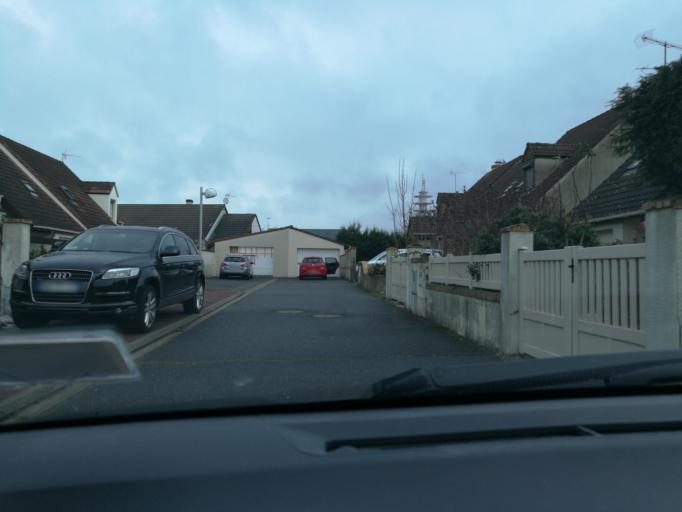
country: FR
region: Centre
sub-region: Departement du Loiret
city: Fleury-les-Aubrais
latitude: 47.9388
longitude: 1.9252
